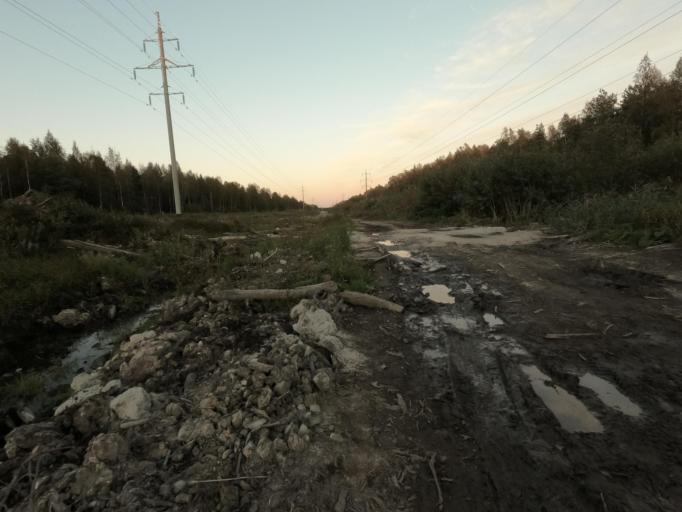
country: RU
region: Leningrad
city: Otradnoye
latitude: 59.7679
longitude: 30.8339
